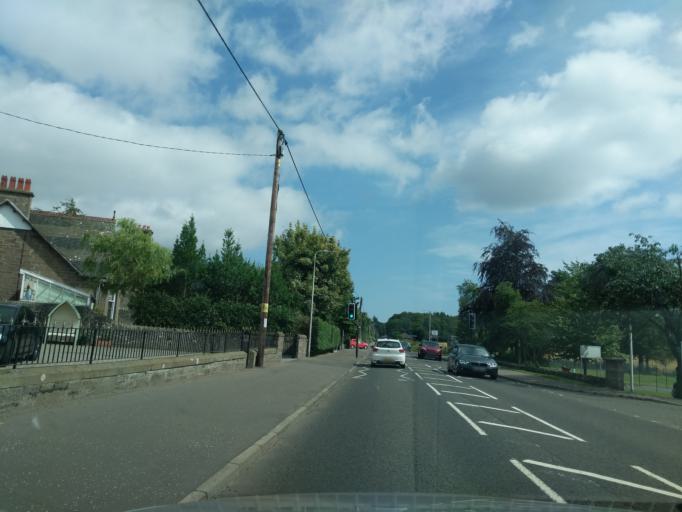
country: GB
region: Scotland
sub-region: Angus
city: Muirhead
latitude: 56.4946
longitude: -3.0594
